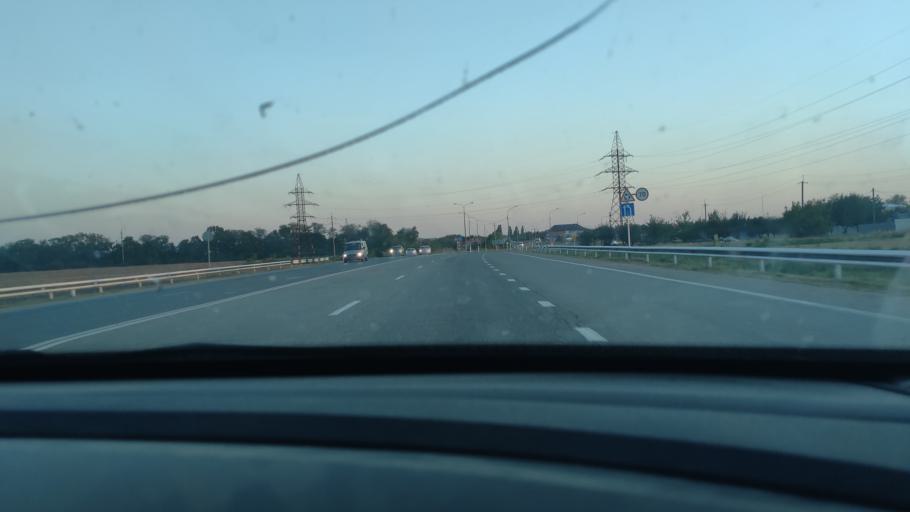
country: RU
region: Krasnodarskiy
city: Timashevsk
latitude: 45.6126
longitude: 38.9871
